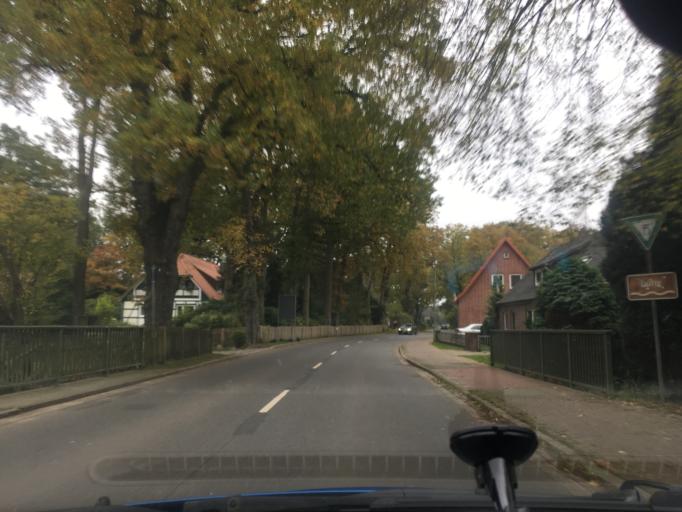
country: DE
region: Lower Saxony
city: Bispingen
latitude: 53.0961
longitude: 10.0263
